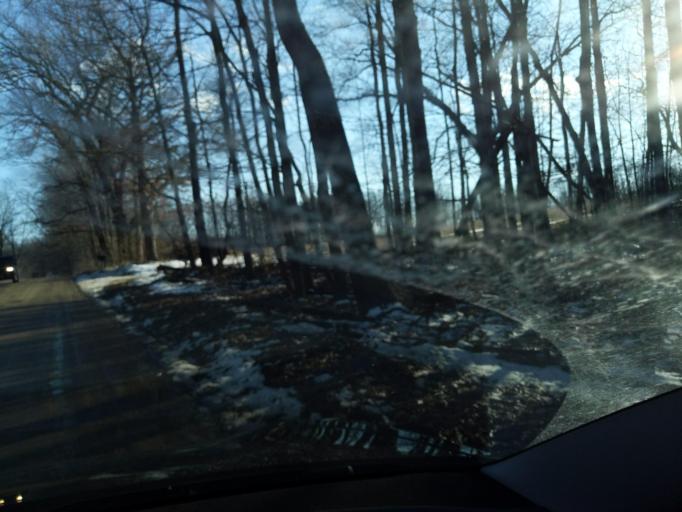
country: US
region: Michigan
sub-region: Ingham County
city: Stockbridge
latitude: 42.5228
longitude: -84.1414
